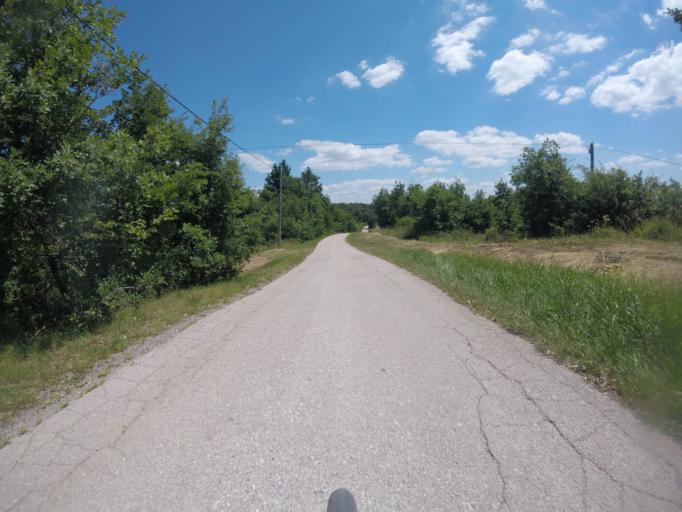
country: SI
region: Metlika
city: Metlika
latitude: 45.6955
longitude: 15.3886
